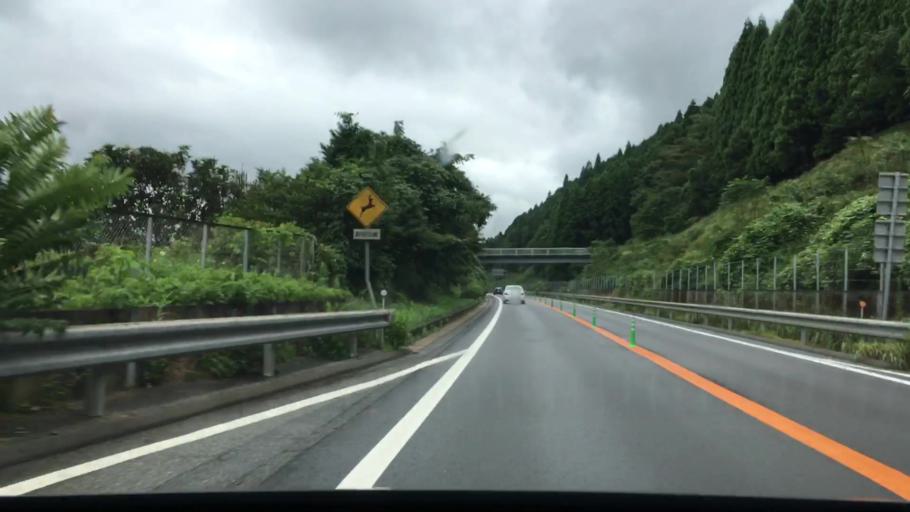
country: JP
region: Hyogo
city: Nishiwaki
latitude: 35.1081
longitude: 134.7797
